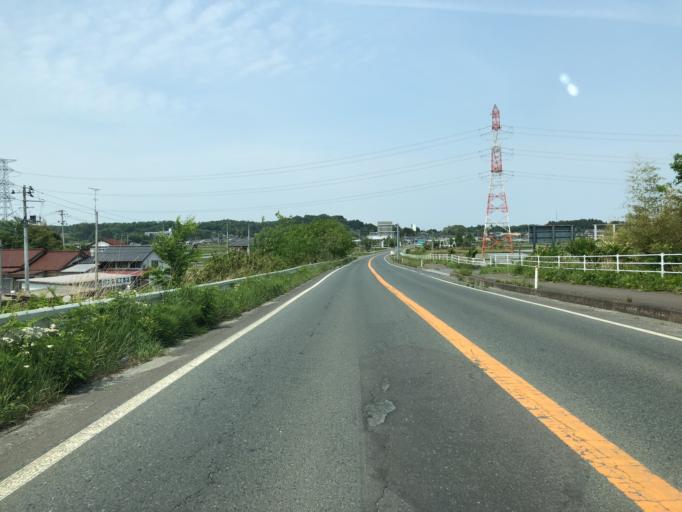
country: JP
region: Miyagi
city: Marumori
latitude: 37.8388
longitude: 140.9181
